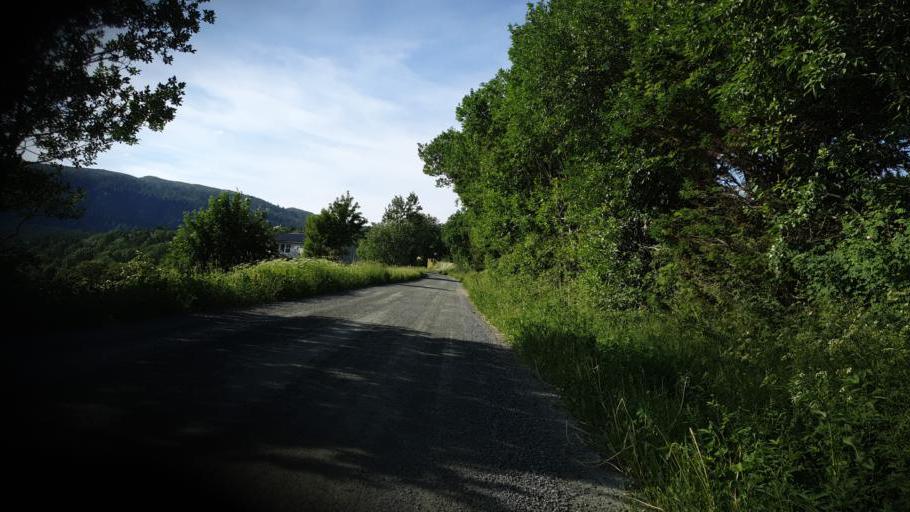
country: NO
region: Sor-Trondelag
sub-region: Trondheim
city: Trondheim
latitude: 63.5707
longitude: 10.4068
